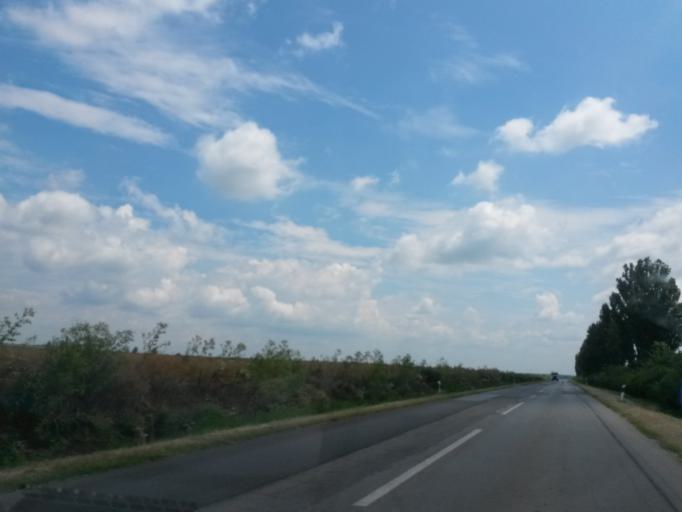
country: HR
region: Osjecko-Baranjska
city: Dalj
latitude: 45.5110
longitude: 18.9322
